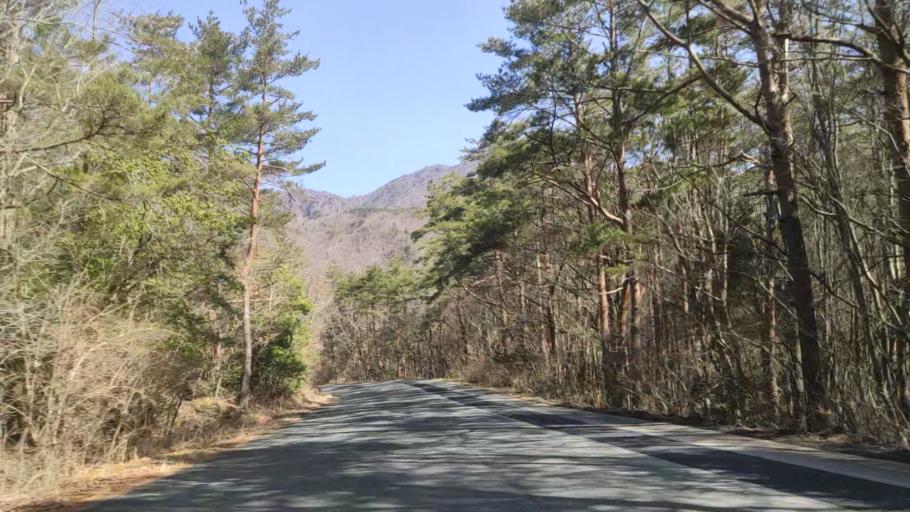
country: JP
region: Yamanashi
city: Fujikawaguchiko
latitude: 35.4950
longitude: 138.6688
